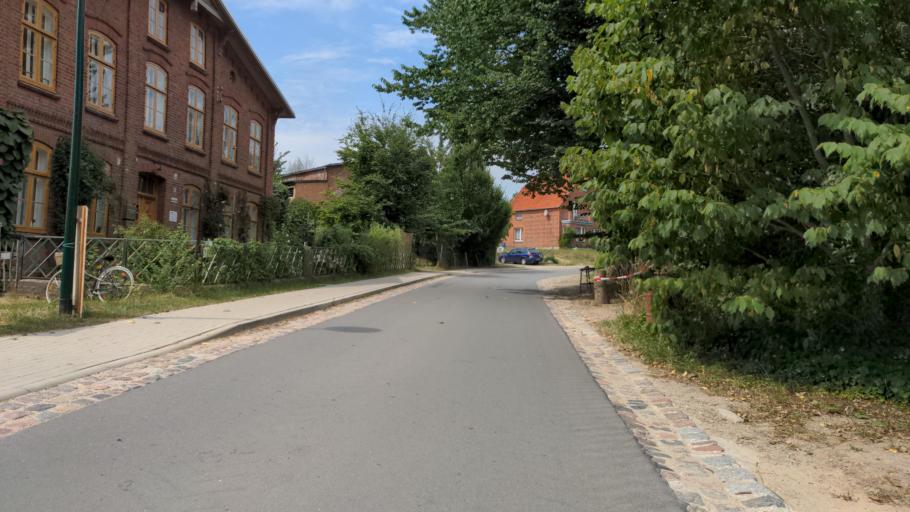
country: DE
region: Mecklenburg-Vorpommern
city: Selmsdorf
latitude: 53.8535
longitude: 10.8014
